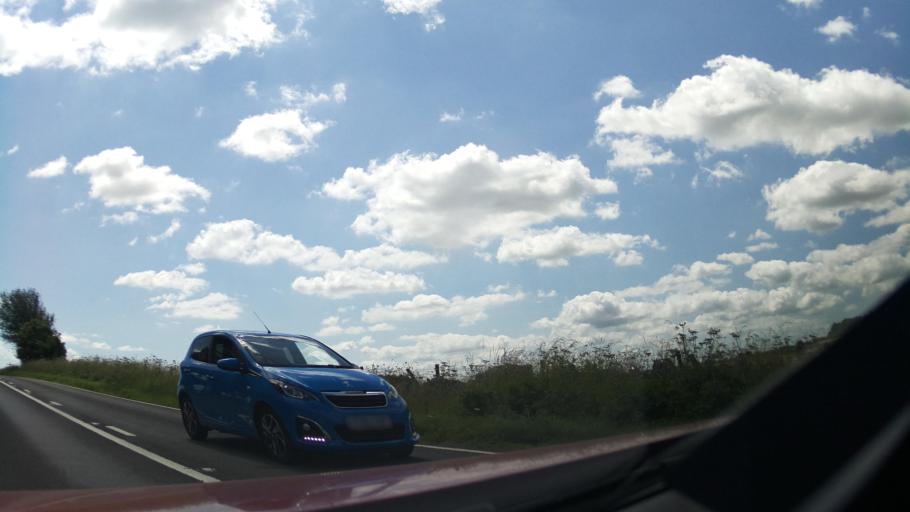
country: GB
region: England
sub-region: Derbyshire
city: Bakewell
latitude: 53.1563
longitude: -1.7714
